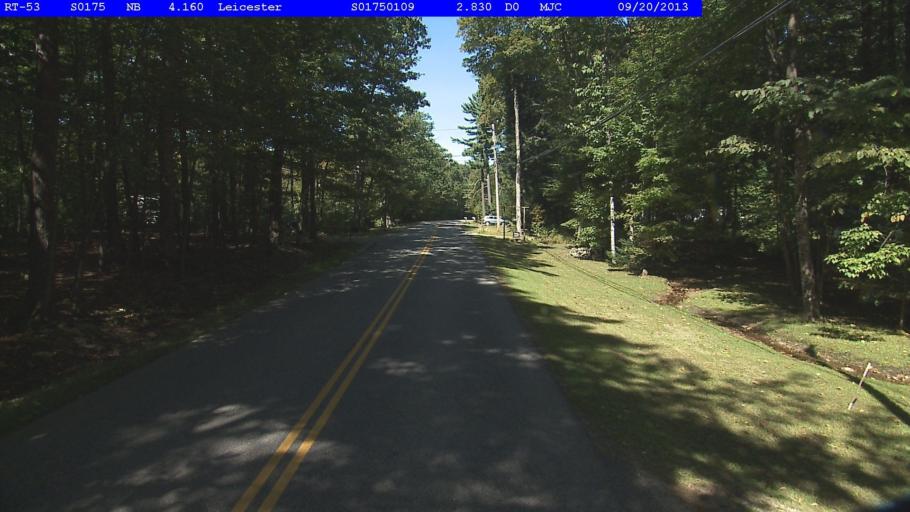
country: US
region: Vermont
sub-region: Rutland County
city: Brandon
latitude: 43.8834
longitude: -73.0638
